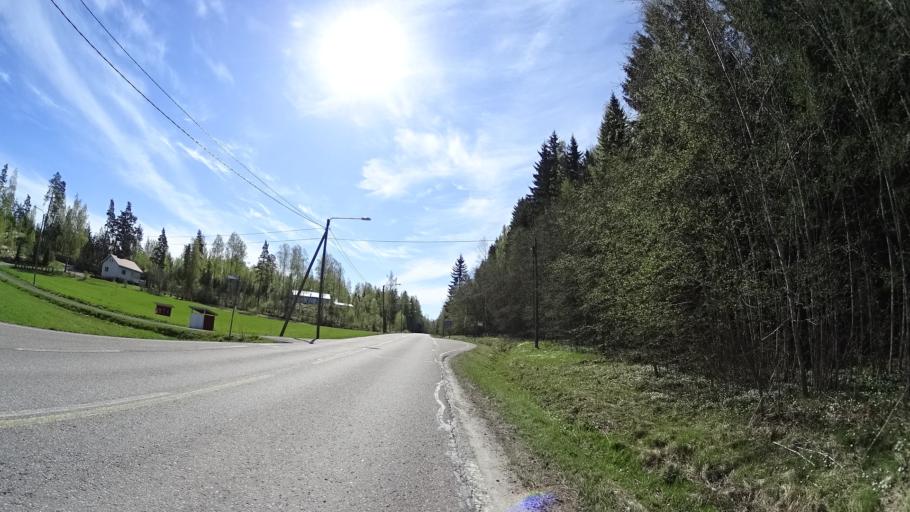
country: FI
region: Uusimaa
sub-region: Helsinki
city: Nurmijaervi
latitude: 60.3927
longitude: 24.8333
